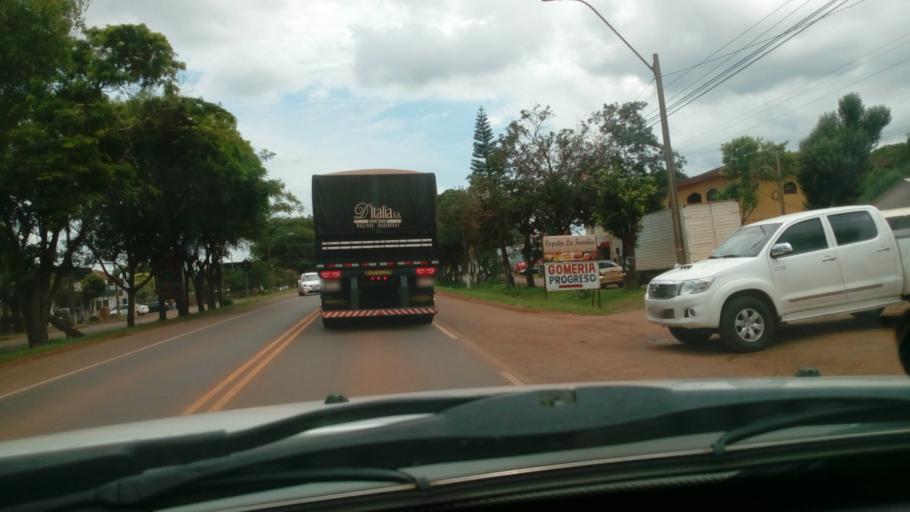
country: PY
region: Alto Parana
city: Santa Rita
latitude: -25.7838
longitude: -55.0798
